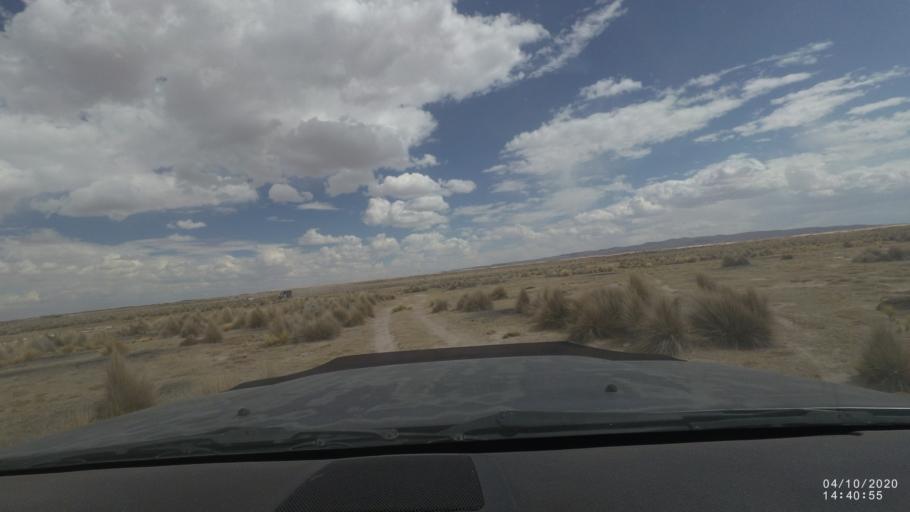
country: BO
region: Oruro
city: Poopo
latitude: -18.6808
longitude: -67.4913
